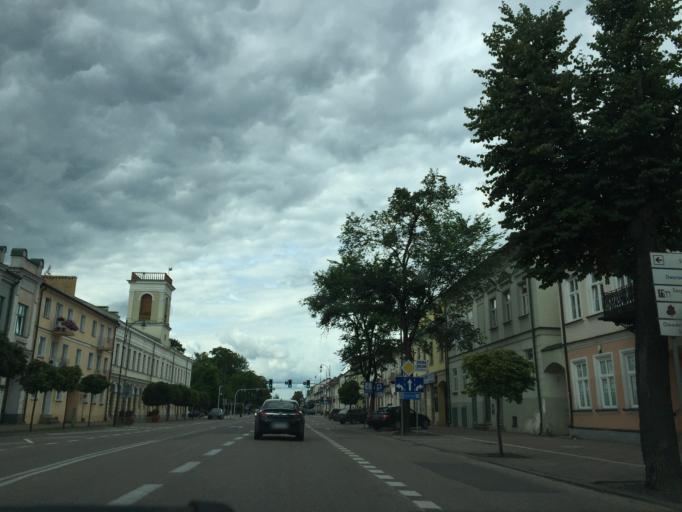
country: PL
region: Podlasie
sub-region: Suwalki
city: Suwalki
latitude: 54.0978
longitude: 22.9286
